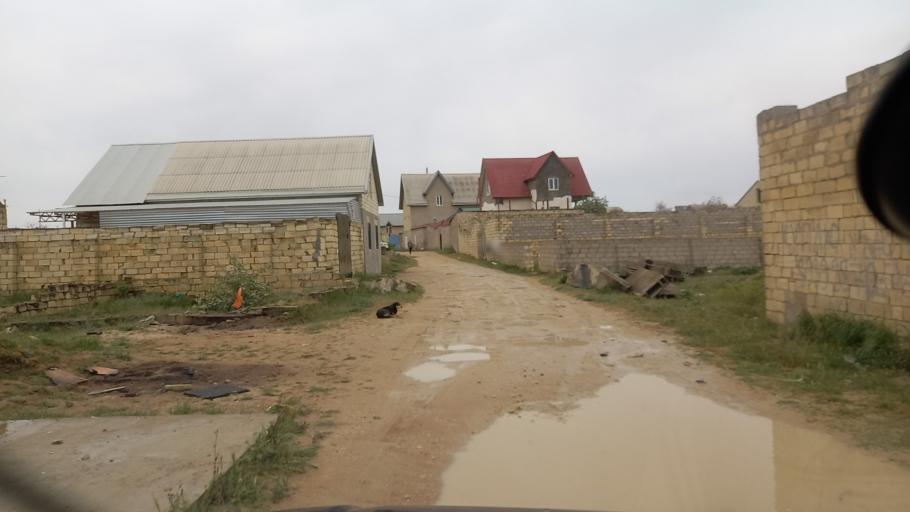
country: RU
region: Dagestan
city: Sabnova
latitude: 42.1204
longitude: 48.2639
